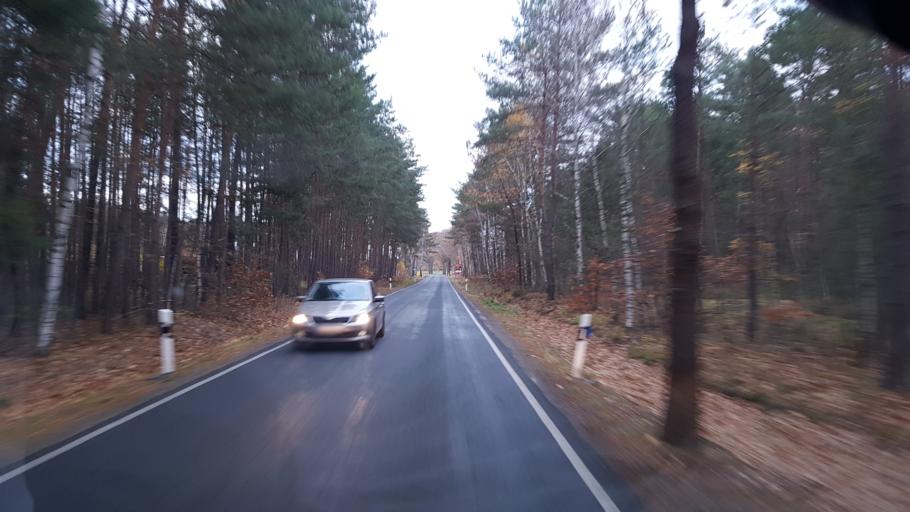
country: DE
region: Brandenburg
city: Ortrand
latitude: 51.4004
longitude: 13.7684
